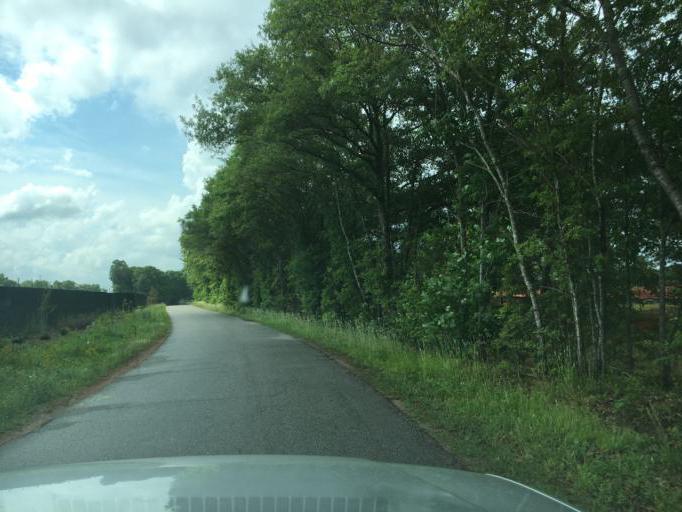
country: US
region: South Carolina
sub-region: Spartanburg County
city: Wellford
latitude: 34.9276
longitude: -82.0570
